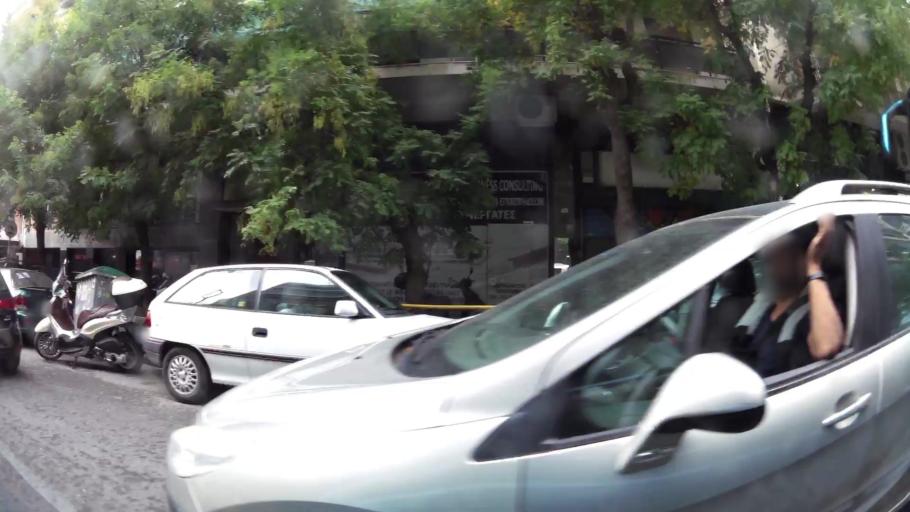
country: GR
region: Attica
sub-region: Nomarchia Athinas
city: Vyronas
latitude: 37.9664
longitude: 23.7553
